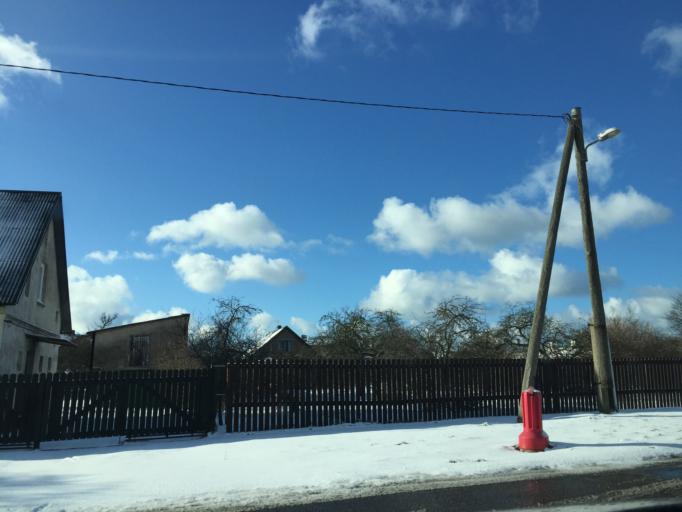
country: LV
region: Ventspils
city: Ventspils
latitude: 57.3846
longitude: 21.5572
